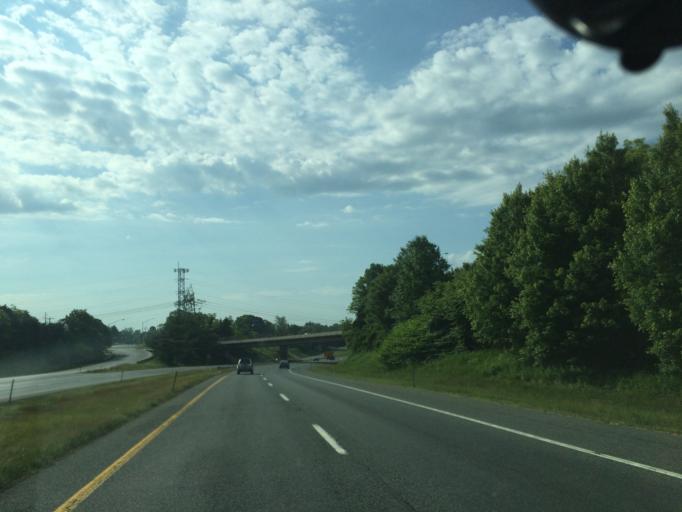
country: US
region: Maryland
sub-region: Baltimore County
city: Reisterstown
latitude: 39.4754
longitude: -76.8413
